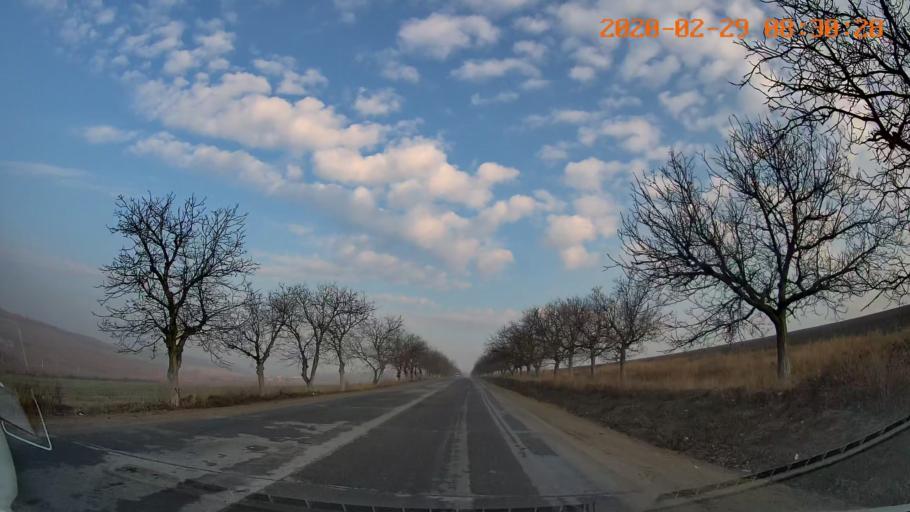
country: MD
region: Anenii Noi
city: Anenii Noi
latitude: 46.9027
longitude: 29.2947
